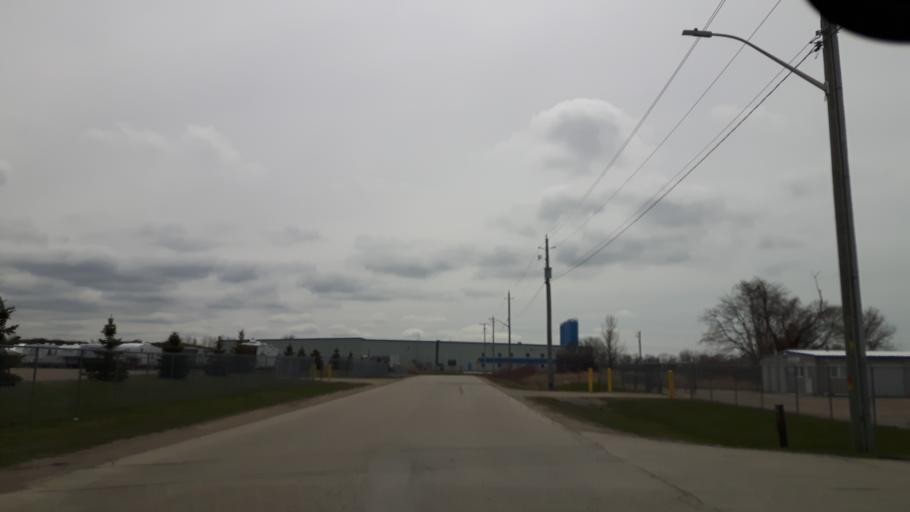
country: CA
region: Ontario
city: Goderich
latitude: 43.7243
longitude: -81.7030
